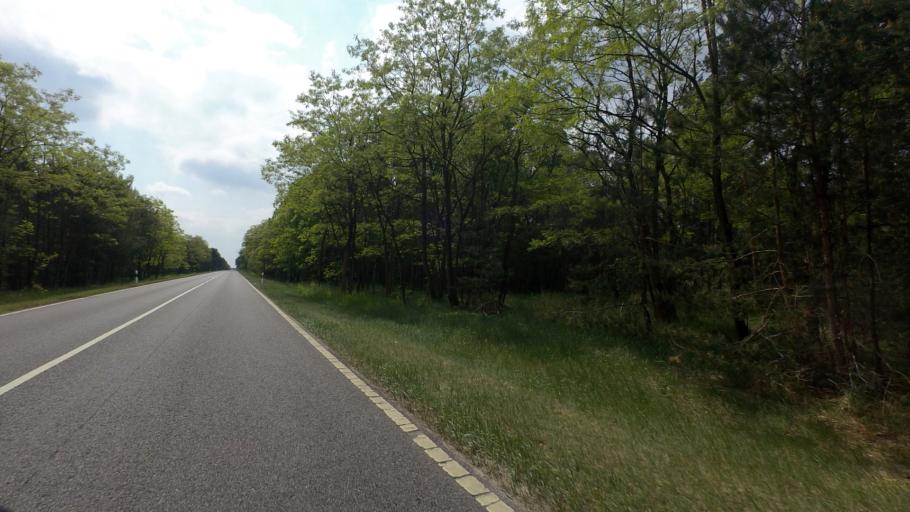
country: DE
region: Brandenburg
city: Lieberose
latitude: 51.9497
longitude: 14.3338
